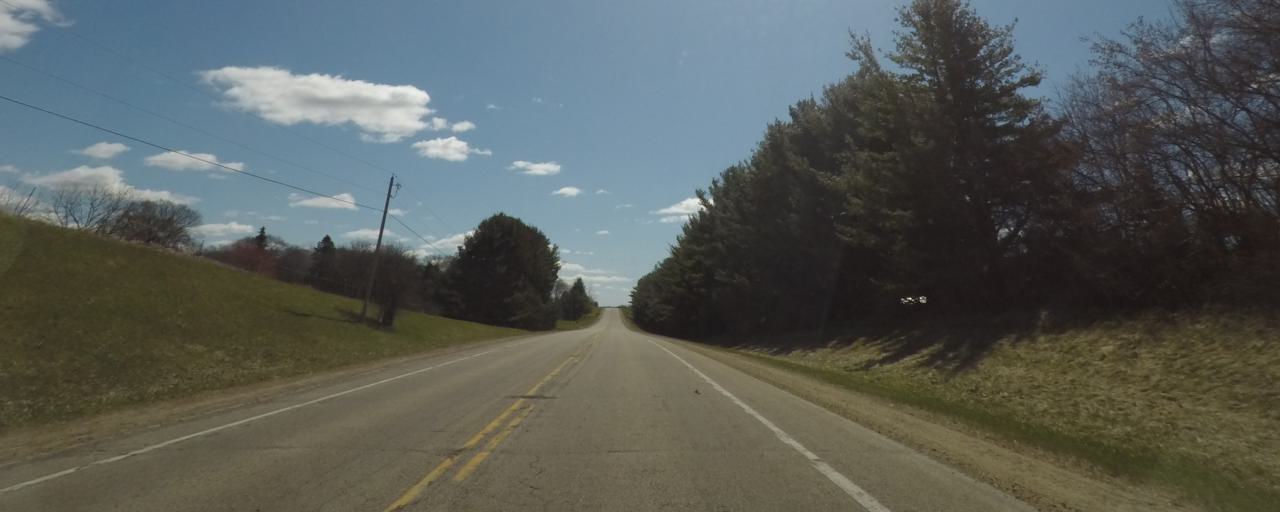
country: US
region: Wisconsin
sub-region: Dane County
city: Cottage Grove
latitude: 43.0818
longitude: -89.1586
